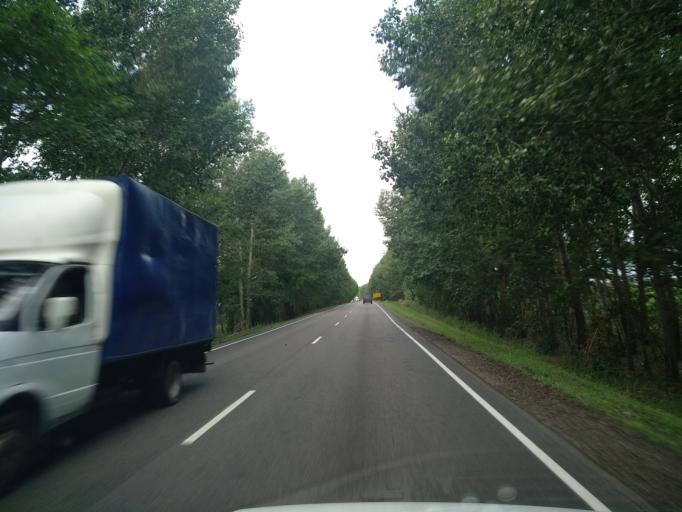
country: RU
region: Voronezj
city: Pereleshino
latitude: 51.8027
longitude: 40.1689
